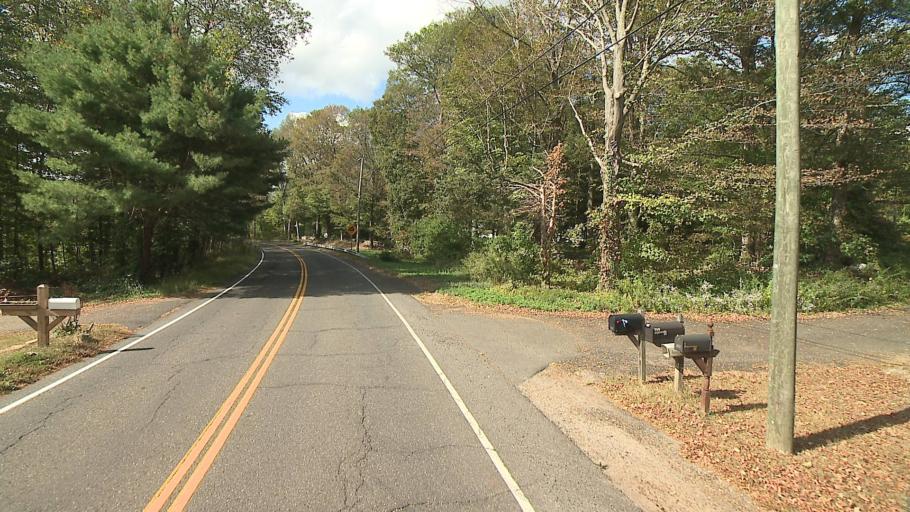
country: US
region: Connecticut
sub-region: New Haven County
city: Naugatuck
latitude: 41.4494
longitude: -73.0317
